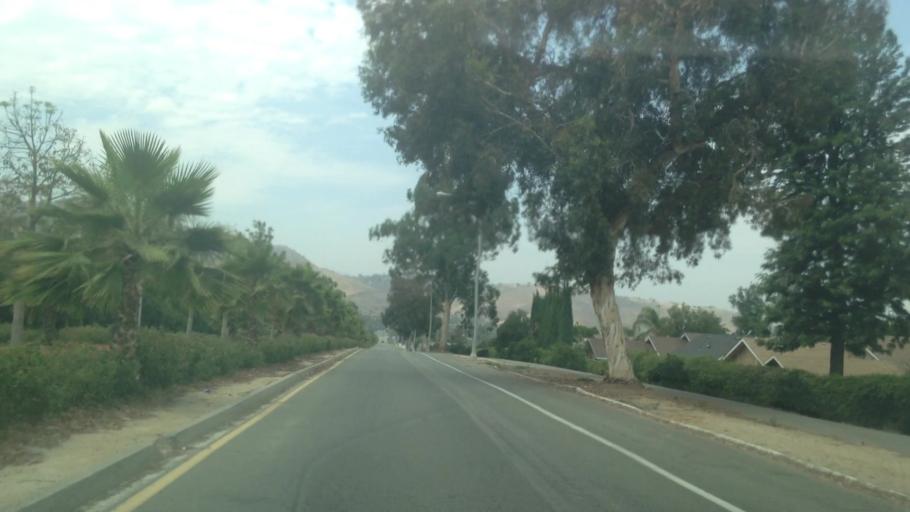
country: US
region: California
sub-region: Riverside County
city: Home Gardens
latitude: 33.8929
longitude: -117.4547
